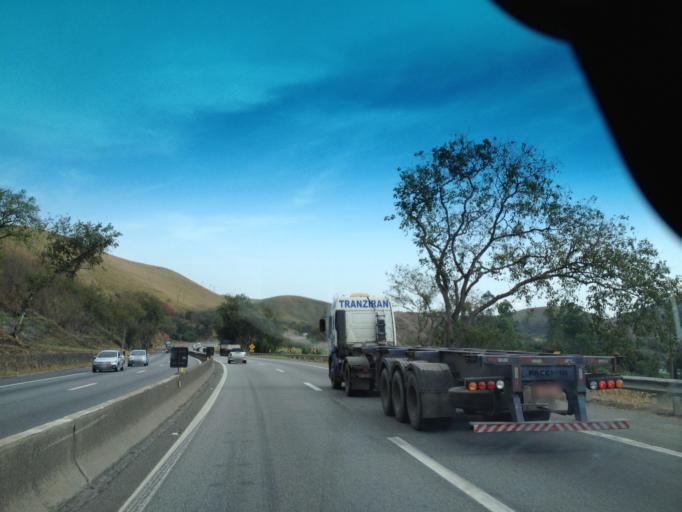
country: BR
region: Rio de Janeiro
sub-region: Porto Real
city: Porto Real
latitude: -22.4842
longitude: -44.2573
